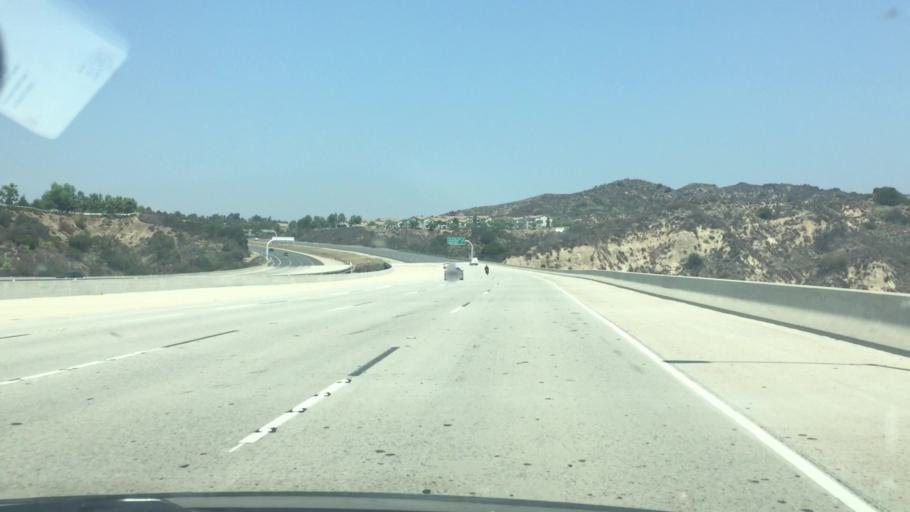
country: US
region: California
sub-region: Orange County
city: Rancho Santa Margarita
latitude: 33.6465
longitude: -117.6055
